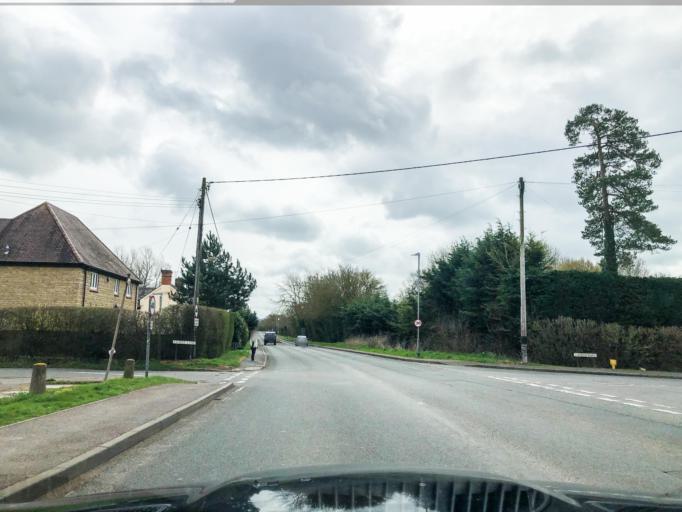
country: GB
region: England
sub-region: Warwickshire
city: Harbury
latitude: 52.1838
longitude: -1.4659
